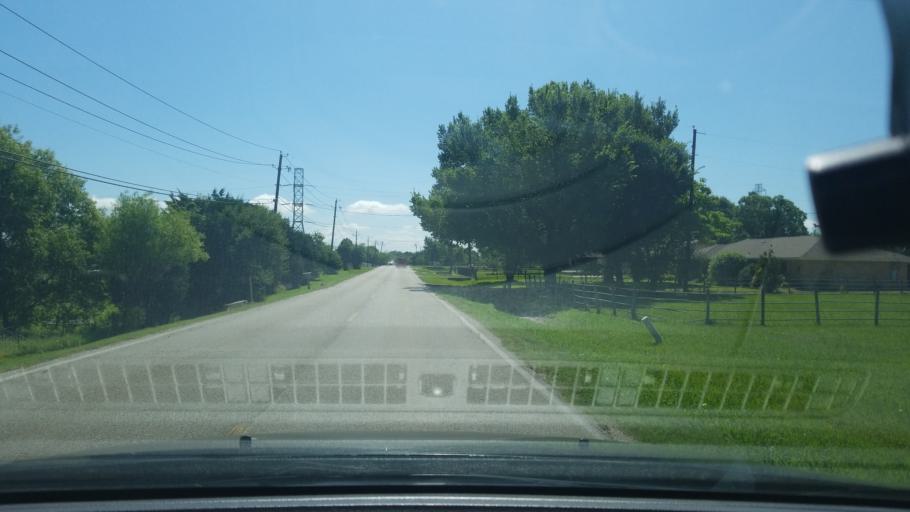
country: US
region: Texas
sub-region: Dallas County
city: Sunnyvale
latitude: 32.7961
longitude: -96.5751
